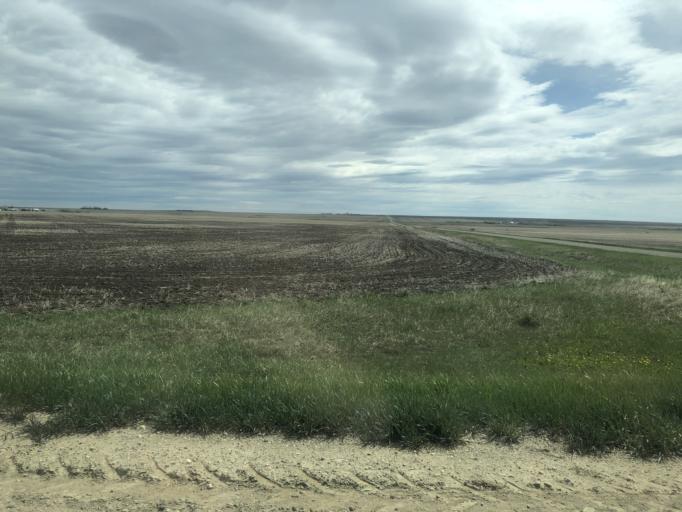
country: CA
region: Alberta
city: Vulcan
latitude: 50.3246
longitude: -113.3231
